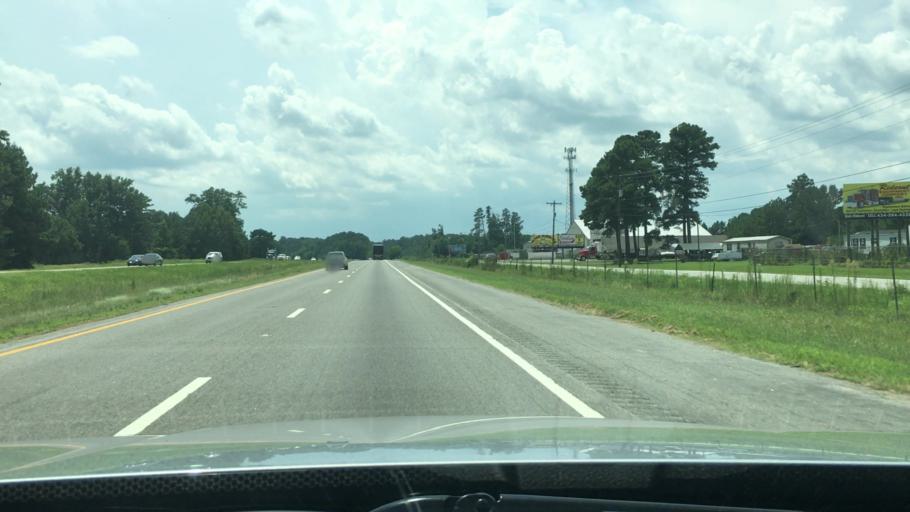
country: US
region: Virginia
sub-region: City of Emporia
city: Emporia
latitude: 36.8321
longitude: -77.4485
